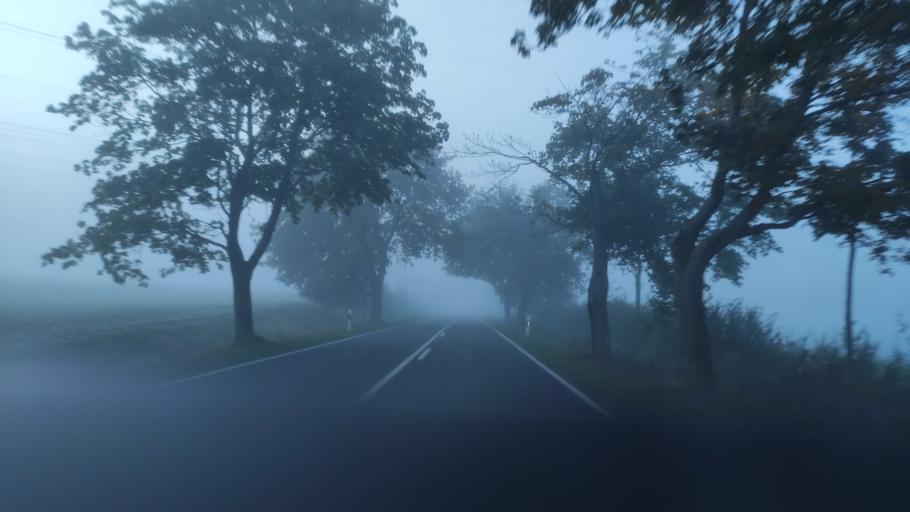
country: DE
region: Mecklenburg-Vorpommern
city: Grabowhofe
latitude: 53.5934
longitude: 12.6212
